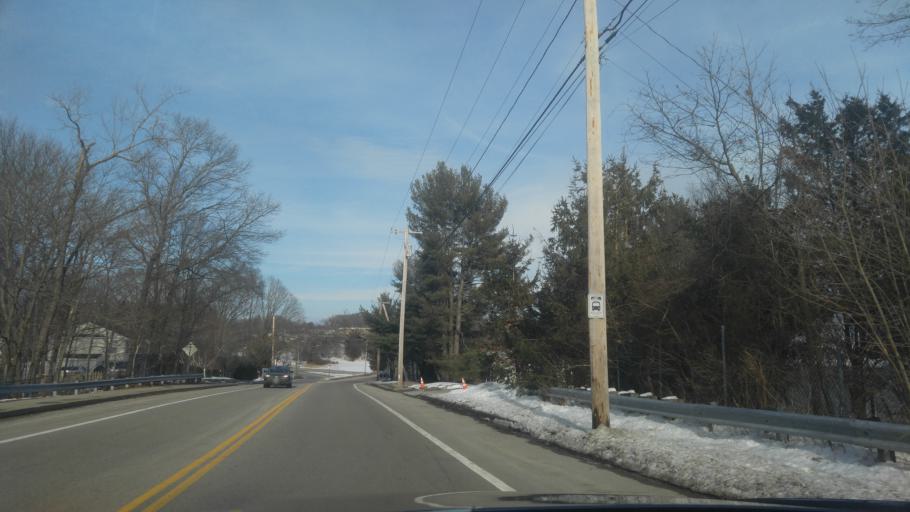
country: US
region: Rhode Island
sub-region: Kent County
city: West Warwick
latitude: 41.7345
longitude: -71.4832
